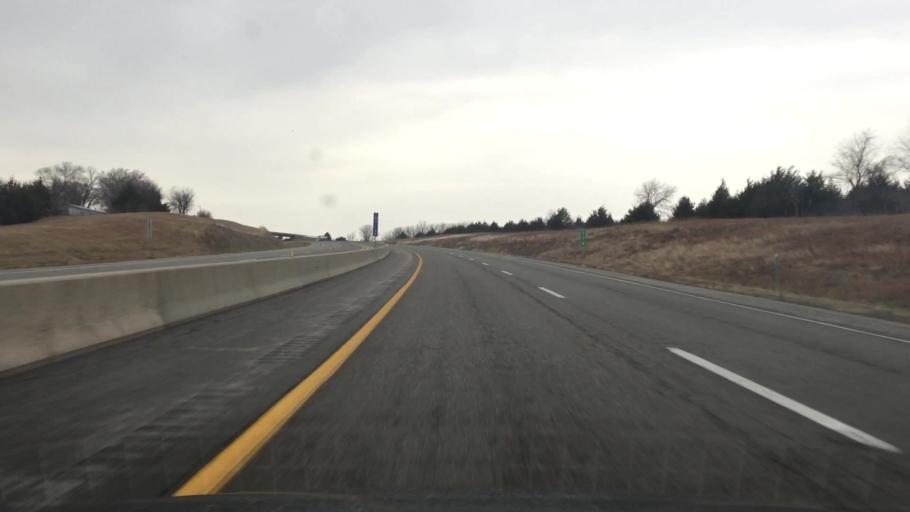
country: US
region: Kansas
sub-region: Shawnee County
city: Auburn
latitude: 38.9598
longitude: -95.7297
